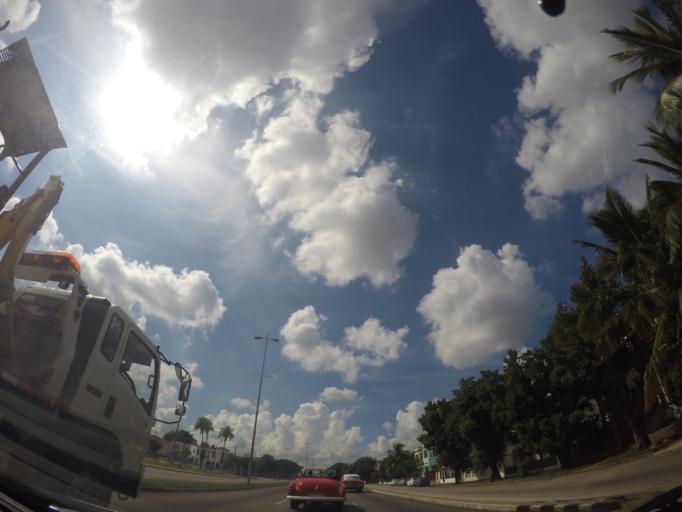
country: CU
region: La Habana
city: Havana
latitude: 23.1154
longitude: -82.4176
